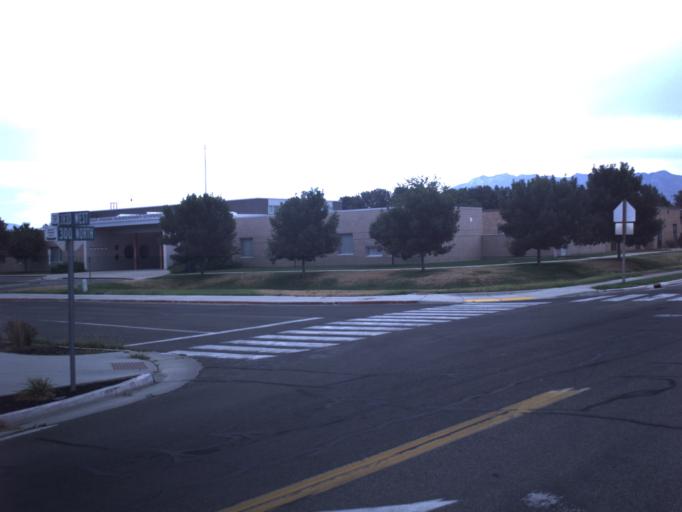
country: US
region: Utah
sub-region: Davis County
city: West Point
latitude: 41.1181
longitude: -112.0998
